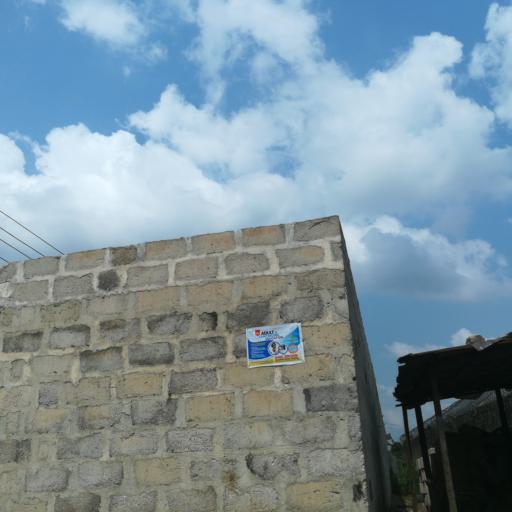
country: NG
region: Rivers
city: Okrika
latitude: 4.8051
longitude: 7.1036
